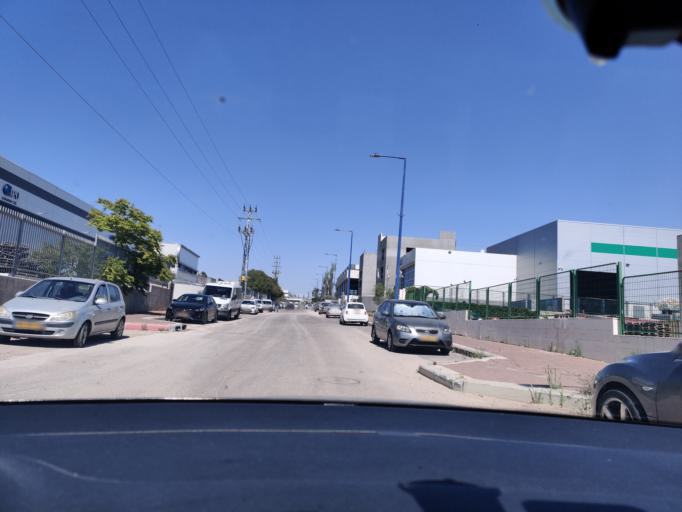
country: IL
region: Southern District
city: Qiryat Gat
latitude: 31.5940
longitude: 34.7809
